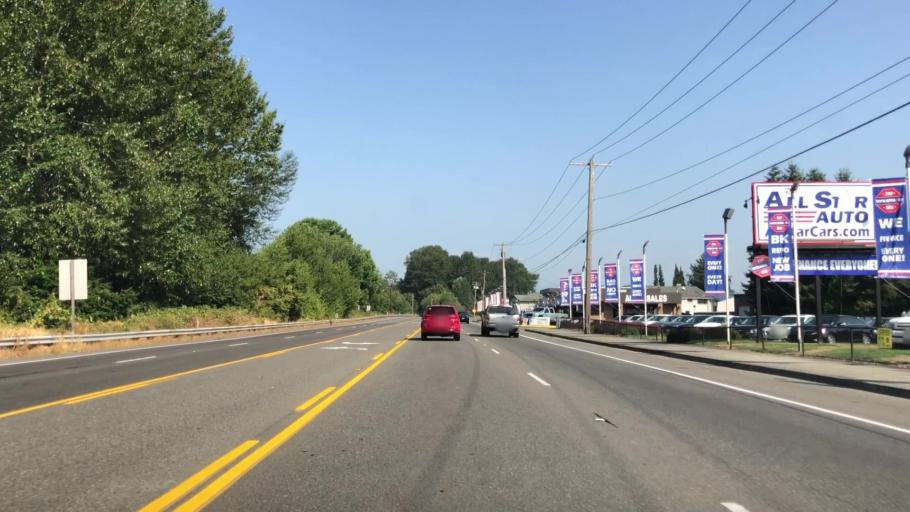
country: US
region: Washington
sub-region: Pierce County
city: Puyallup
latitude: 47.2058
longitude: -122.3181
